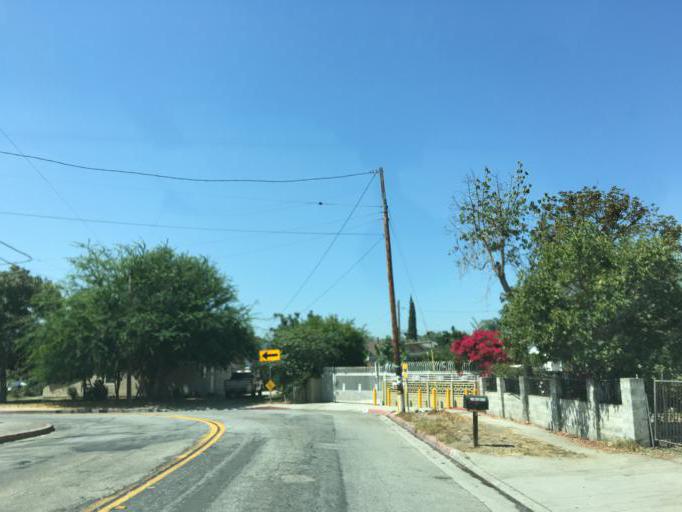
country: US
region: California
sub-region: Los Angeles County
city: Avocado Heights
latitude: 34.0462
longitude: -118.0050
